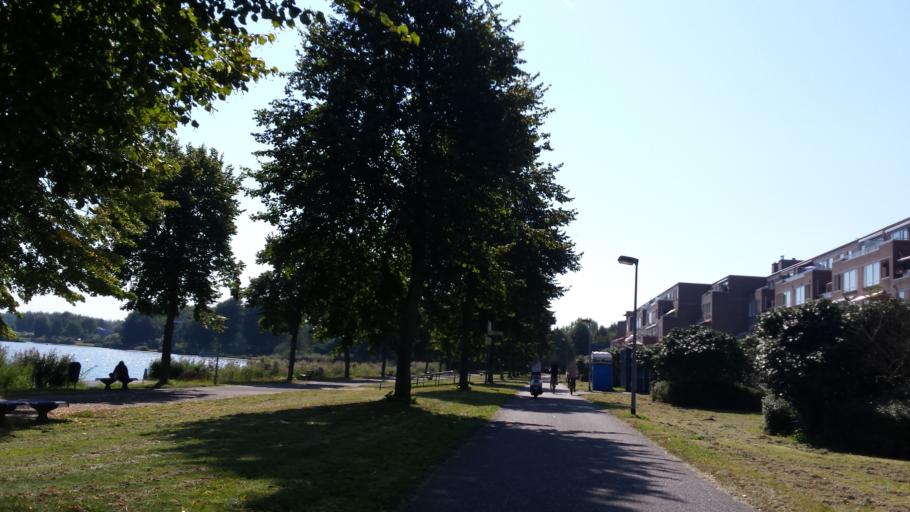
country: NL
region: Flevoland
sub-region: Gemeente Almere
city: Almere Stad
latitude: 52.3630
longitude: 5.2119
